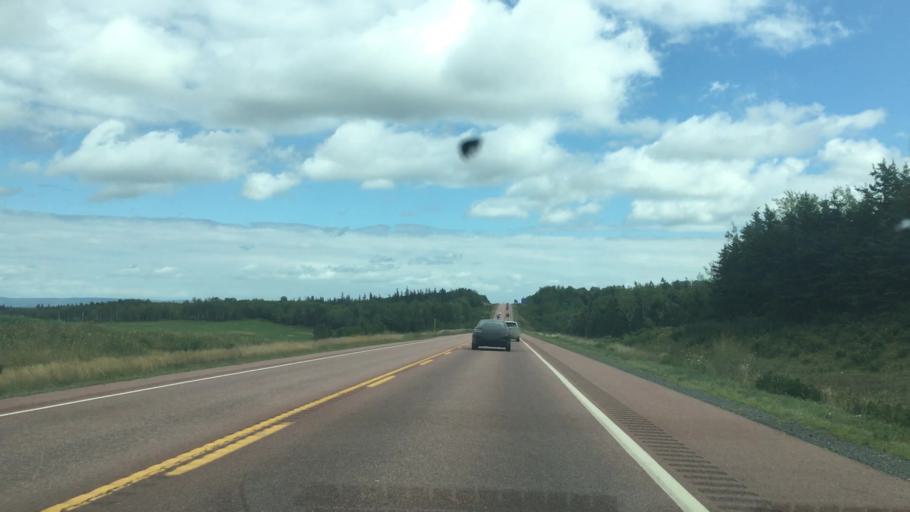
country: CA
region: Nova Scotia
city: Antigonish
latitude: 45.6048
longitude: -61.6833
